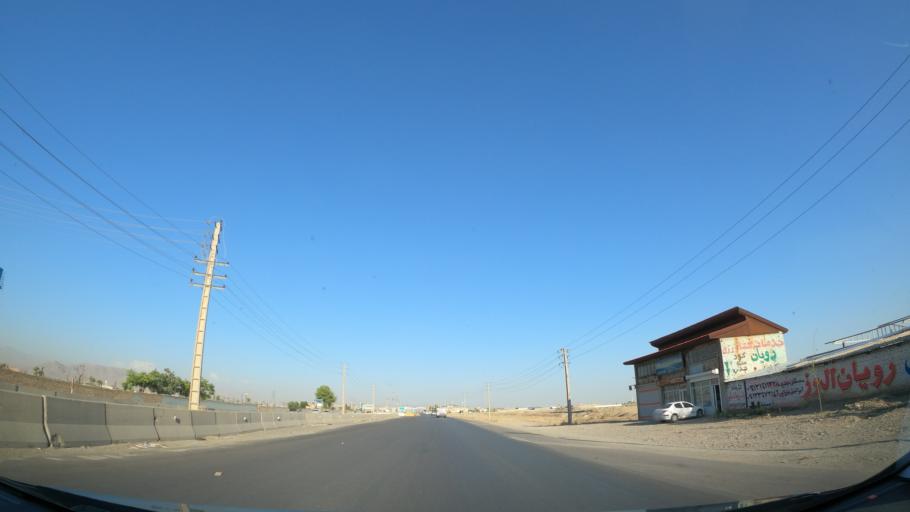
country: IR
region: Alborz
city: Hashtgerd
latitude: 35.9208
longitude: 50.7472
